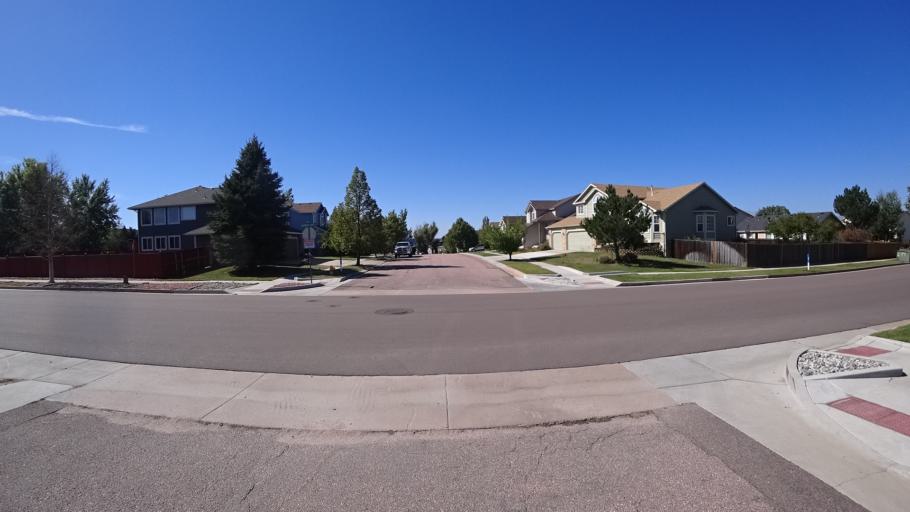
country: US
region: Colorado
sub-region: El Paso County
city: Black Forest
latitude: 38.9531
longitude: -104.7257
